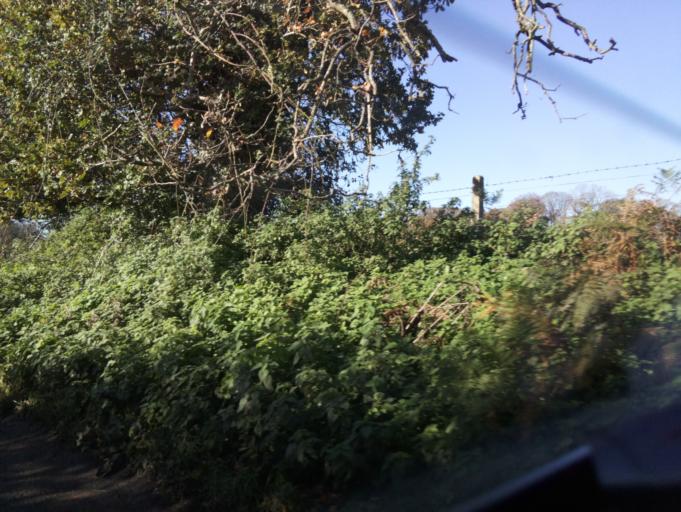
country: GB
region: England
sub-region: Somerset
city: Yeovil
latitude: 50.9305
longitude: -2.6291
